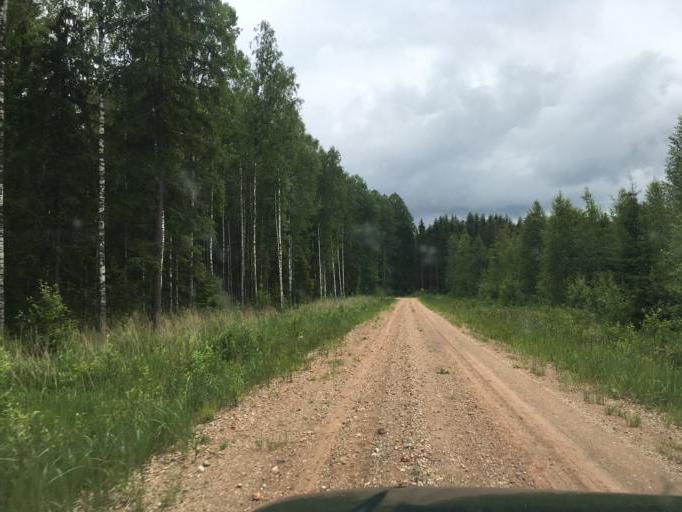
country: LV
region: Vilaka
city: Vilaka
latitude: 57.3824
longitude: 27.5455
